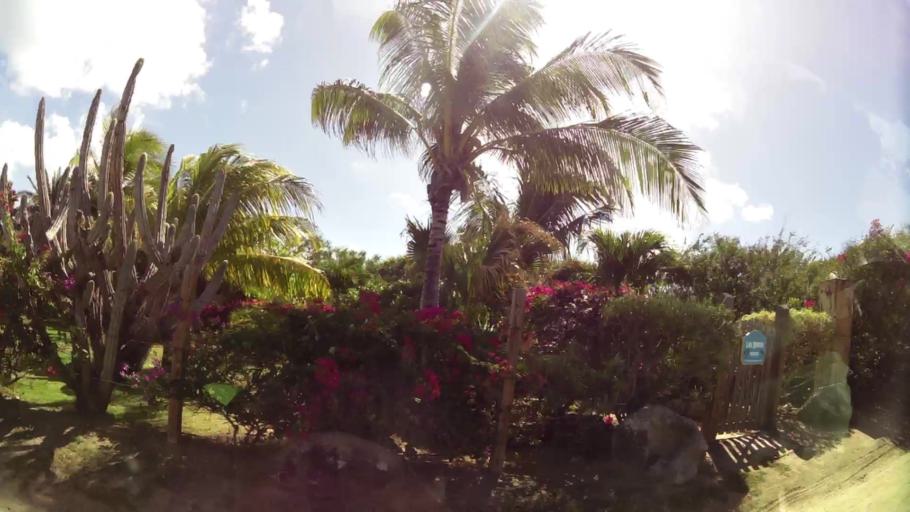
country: VG
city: Tortola
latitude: 18.4291
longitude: -64.4419
